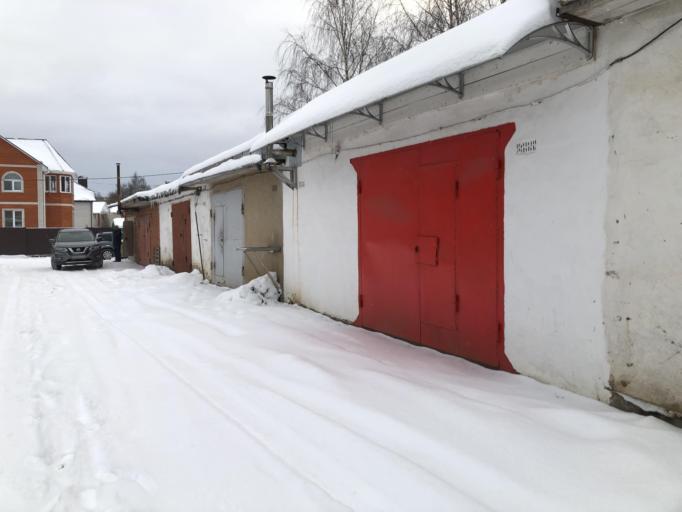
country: RU
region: Smolensk
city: Safonovo
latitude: 55.1142
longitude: 33.2288
